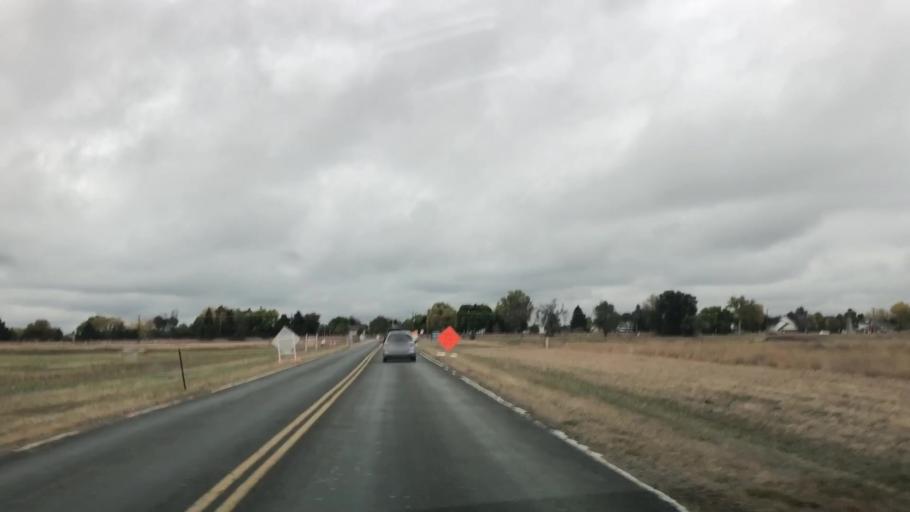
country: US
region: Colorado
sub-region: Larimer County
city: Loveland
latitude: 40.4289
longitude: -105.0167
